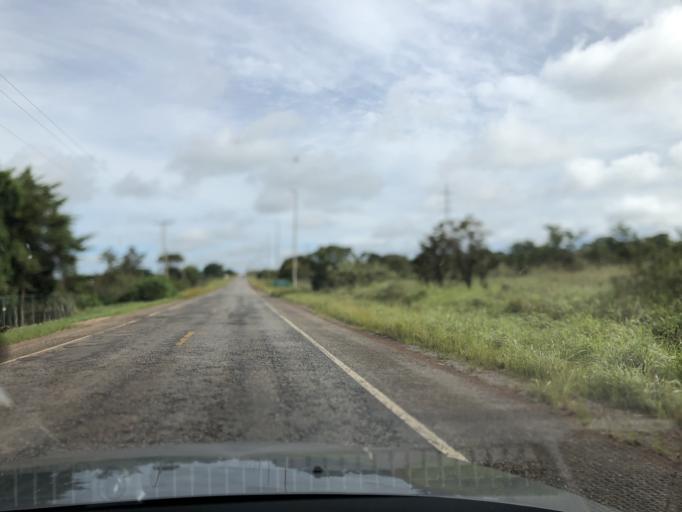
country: BR
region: Federal District
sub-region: Brasilia
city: Brasilia
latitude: -15.7115
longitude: -48.0874
